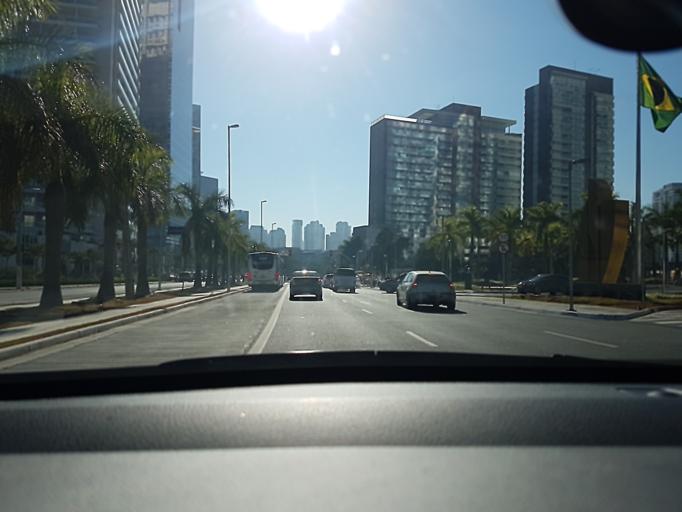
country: BR
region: Sao Paulo
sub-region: Taboao Da Serra
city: Taboao da Serra
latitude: -23.6268
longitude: -46.7029
